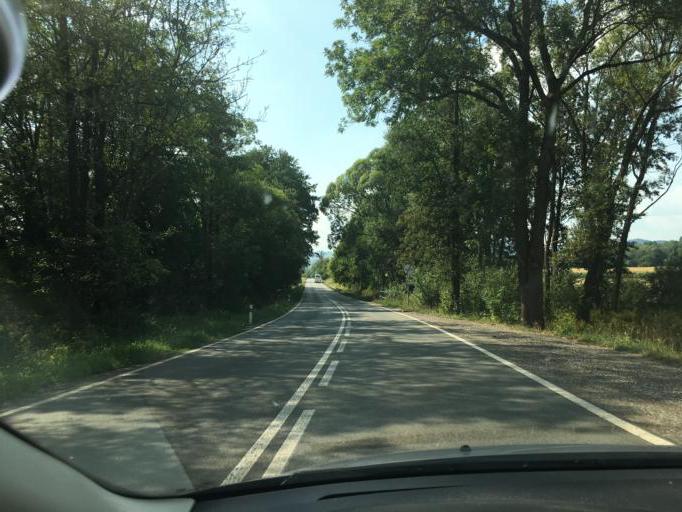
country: CZ
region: Kralovehradecky
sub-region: Okres Trutnov
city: Rudnik
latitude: 50.6161
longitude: 15.6748
